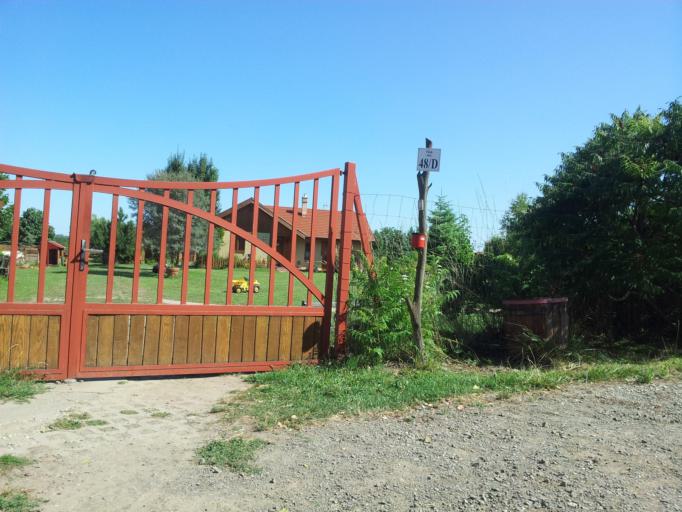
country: HU
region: Pest
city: Veresegyhaz
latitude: 47.6361
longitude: 19.2606
